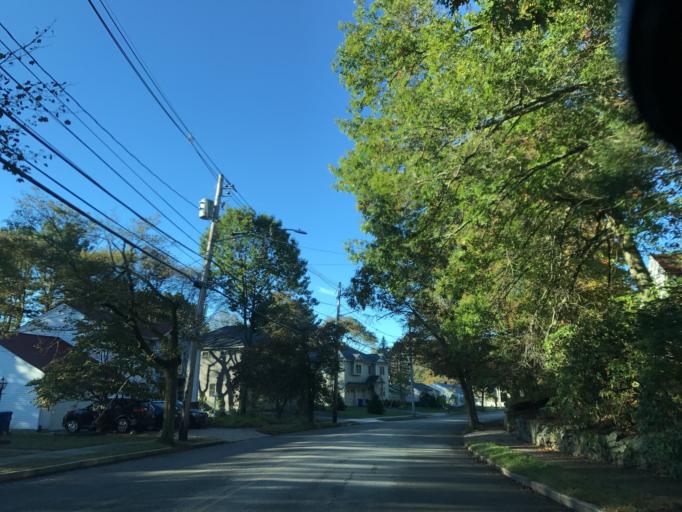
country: US
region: Massachusetts
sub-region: Middlesex County
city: Newton
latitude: 42.2972
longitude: -71.1852
